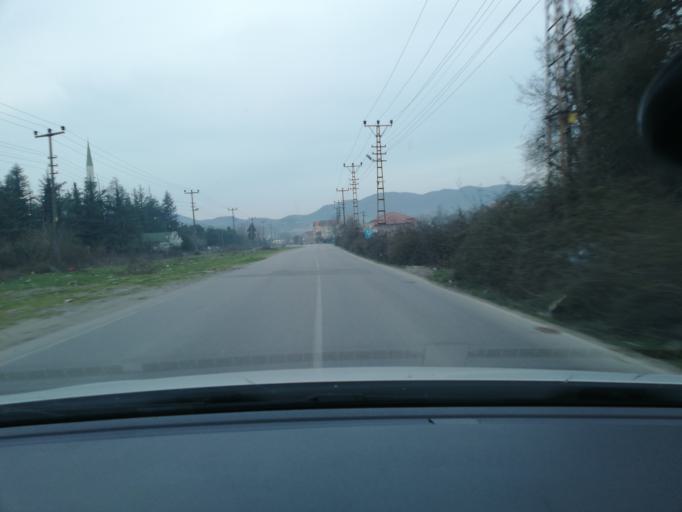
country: TR
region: Zonguldak
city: Caycuma
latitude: 41.4141
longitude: 32.1021
